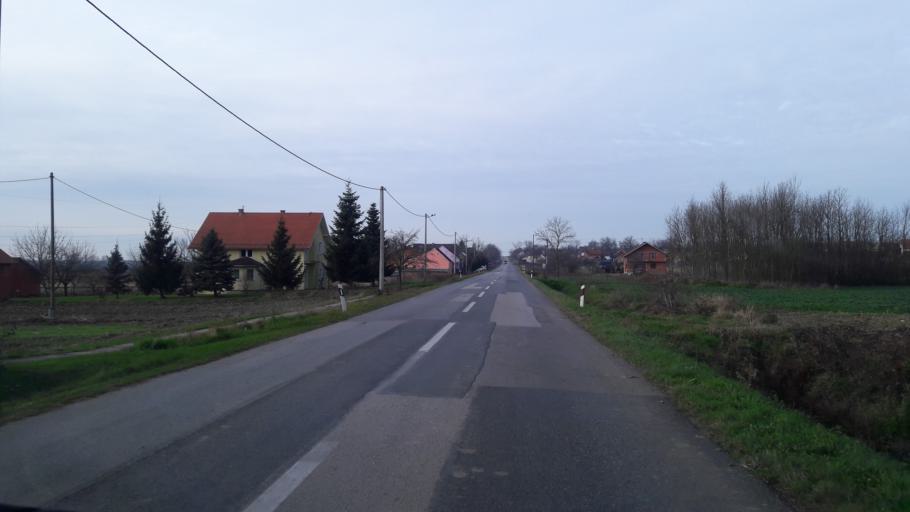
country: HR
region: Osjecko-Baranjska
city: Viskovci
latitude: 45.2877
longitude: 18.5060
